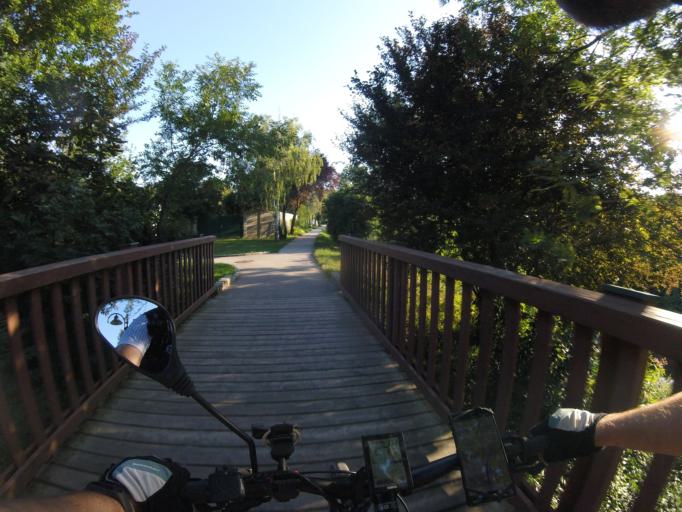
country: AT
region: Lower Austria
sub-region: Politischer Bezirk Baden
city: Trumau
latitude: 47.9958
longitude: 16.3490
